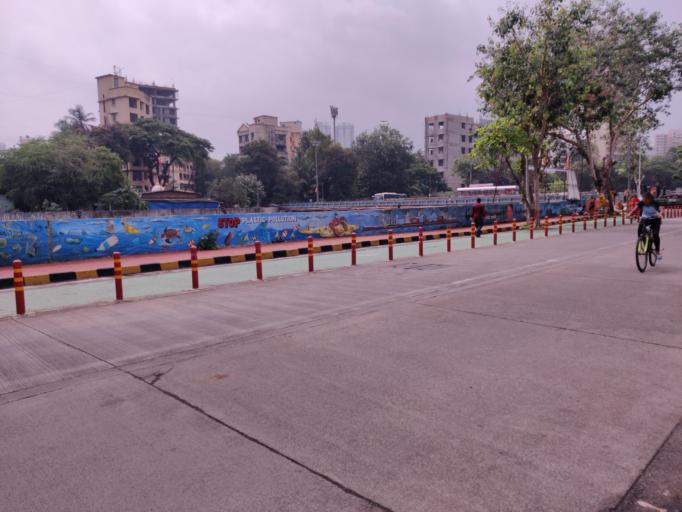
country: IN
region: Maharashtra
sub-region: Mumbai Suburban
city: Borivli
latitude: 19.2557
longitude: 72.8561
